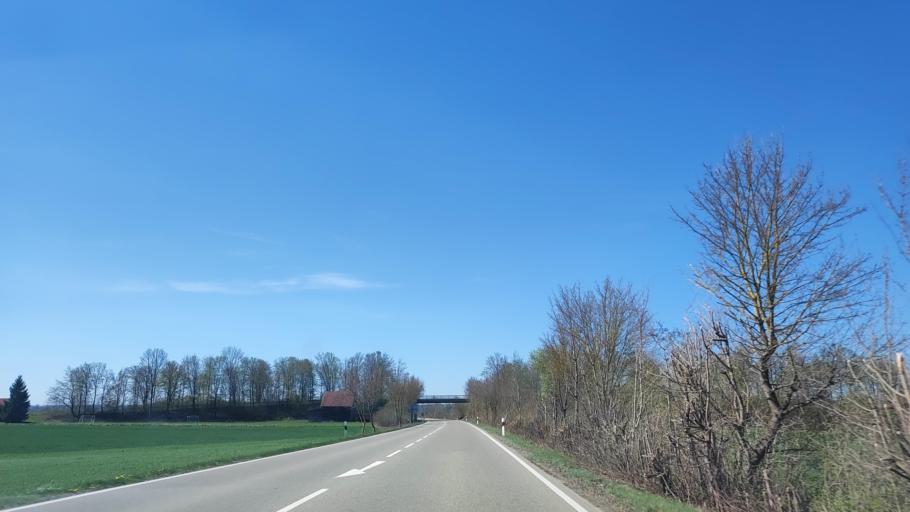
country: DE
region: Bavaria
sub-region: Swabia
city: Kirchheim
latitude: 48.1855
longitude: 10.4689
